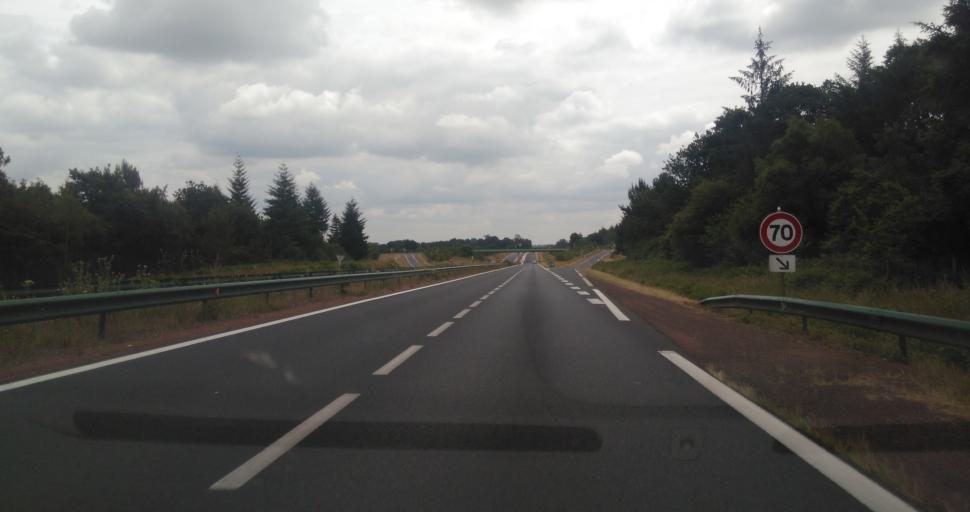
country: FR
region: Pays de la Loire
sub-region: Departement de la Vendee
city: Bournezeau
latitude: 46.6461
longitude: -1.2073
